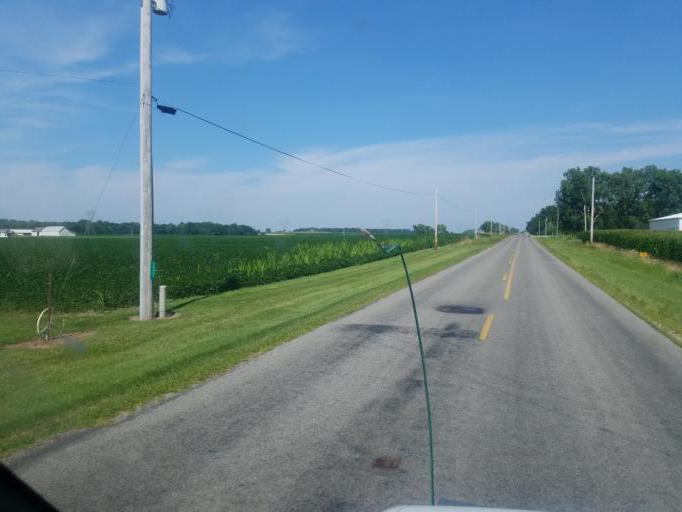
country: US
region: Ohio
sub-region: Shelby County
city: Jackson Center
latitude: 40.4977
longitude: -84.0977
